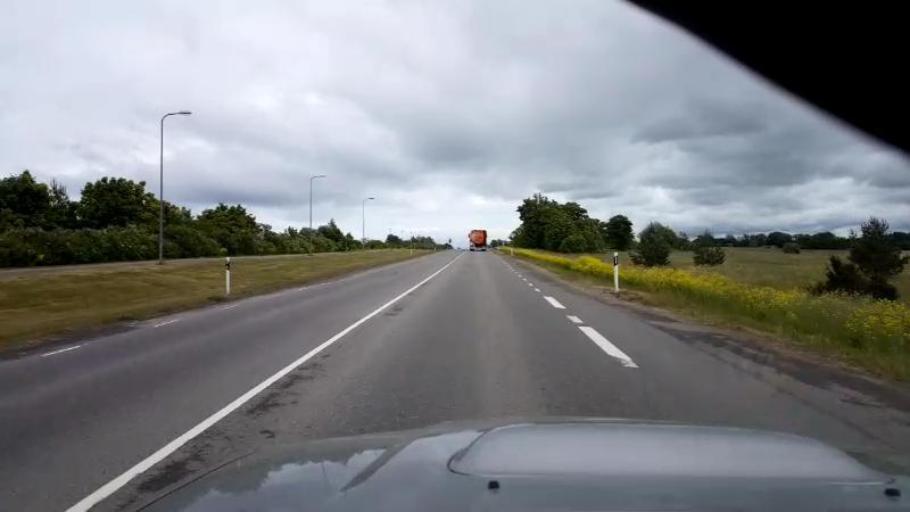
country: EE
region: Harju
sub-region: Harku vald
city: Tabasalu
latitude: 59.4555
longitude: 24.4285
